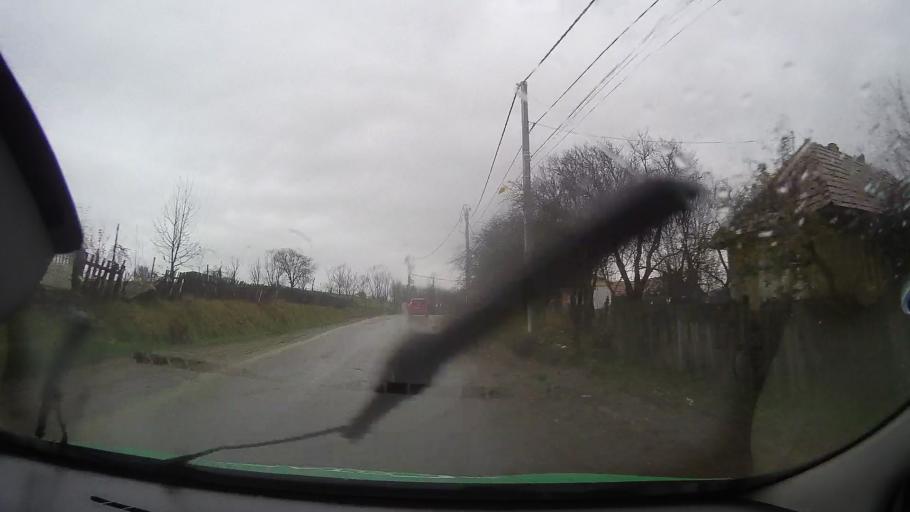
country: RO
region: Mures
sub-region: Comuna Vatava
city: Vatava
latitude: 46.9282
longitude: 24.7689
